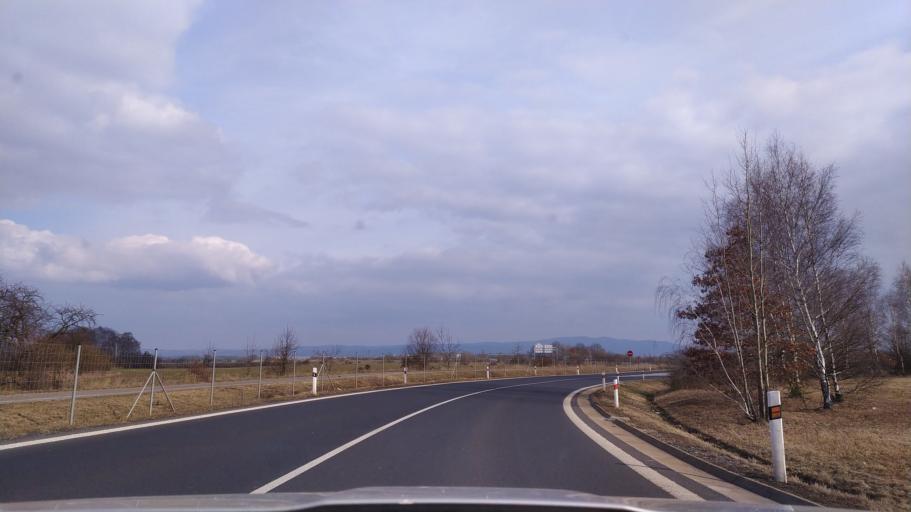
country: CZ
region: Karlovarsky
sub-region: Okres Cheb
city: Cheb
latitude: 50.0886
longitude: 12.4255
